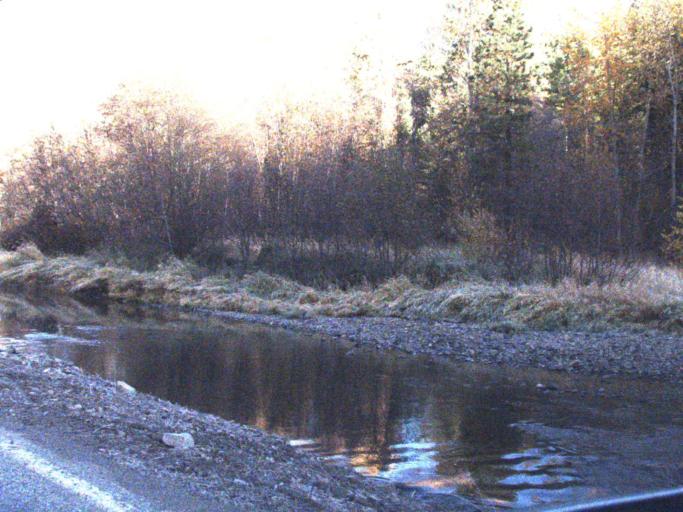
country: US
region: Washington
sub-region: Ferry County
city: Republic
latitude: 48.4321
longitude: -118.7316
